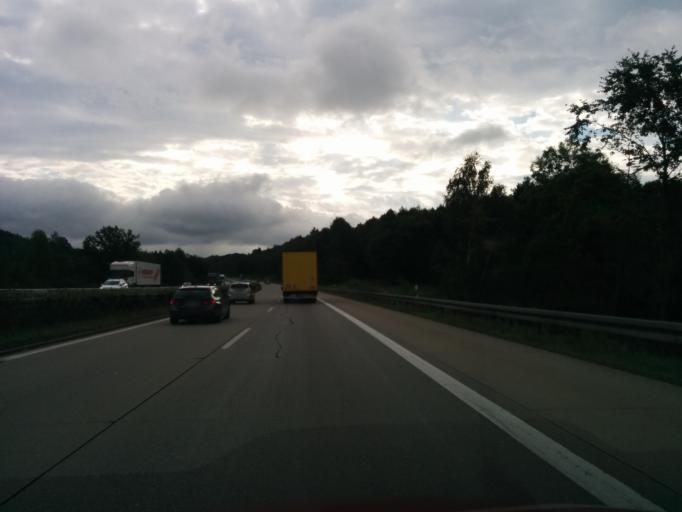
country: DE
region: Bavaria
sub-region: Lower Bavaria
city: Bogen
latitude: 48.9341
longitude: 12.6784
